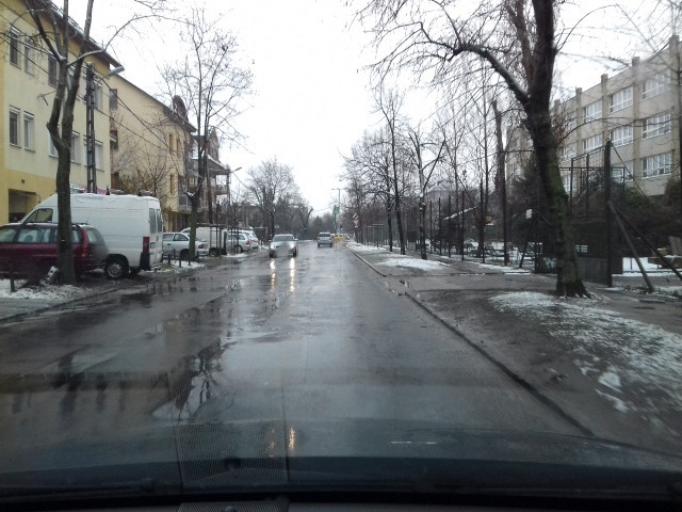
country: HU
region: Budapest
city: Budapest XIV. keruelet
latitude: 47.5180
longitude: 19.1319
